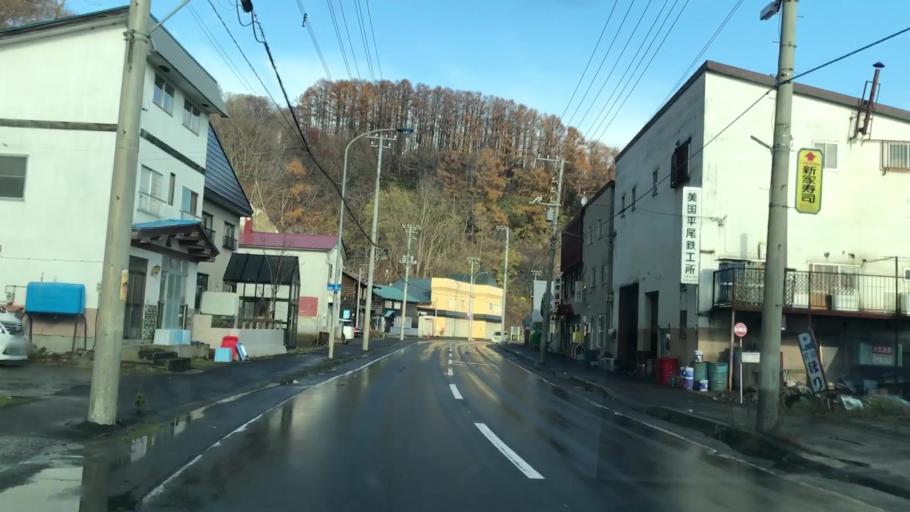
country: JP
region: Hokkaido
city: Yoichi
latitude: 43.2735
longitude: 140.6356
